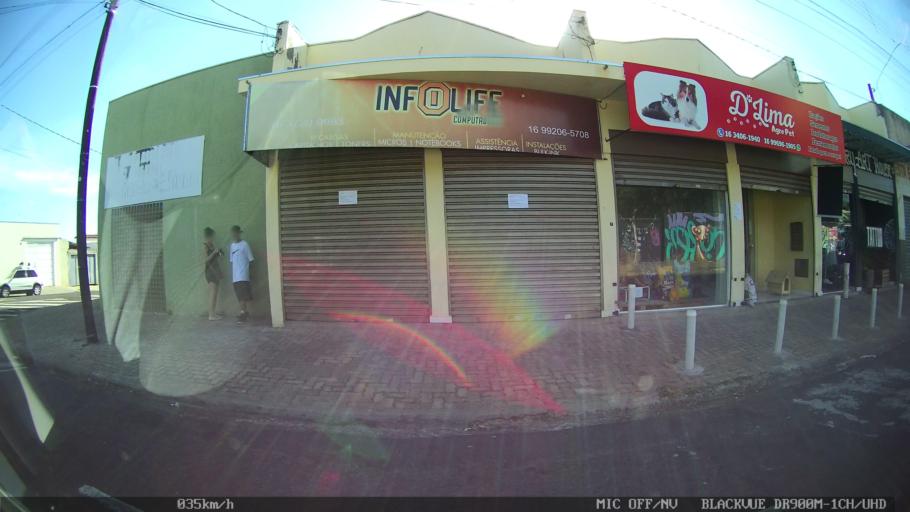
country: BR
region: Sao Paulo
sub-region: Franca
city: Franca
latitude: -20.5001
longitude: -47.4164
